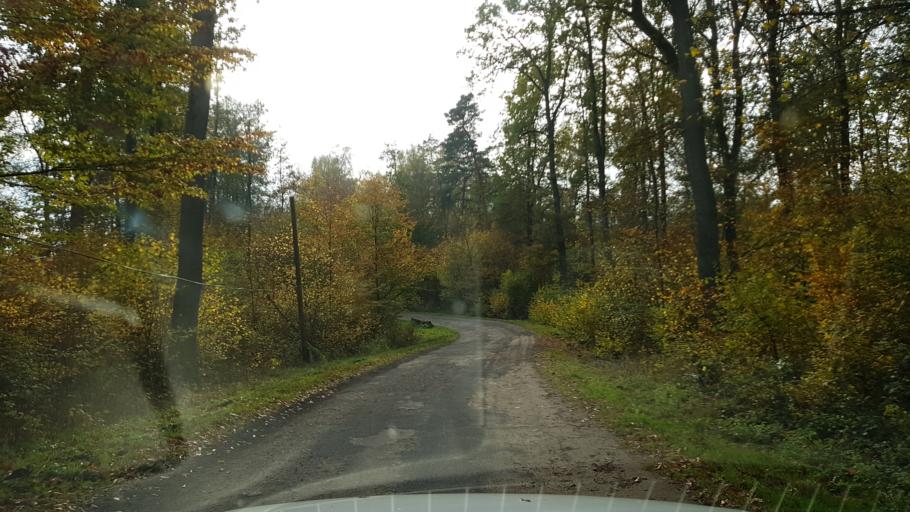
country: PL
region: West Pomeranian Voivodeship
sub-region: Powiat lobeski
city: Wegorzyno
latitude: 53.5056
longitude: 15.4934
